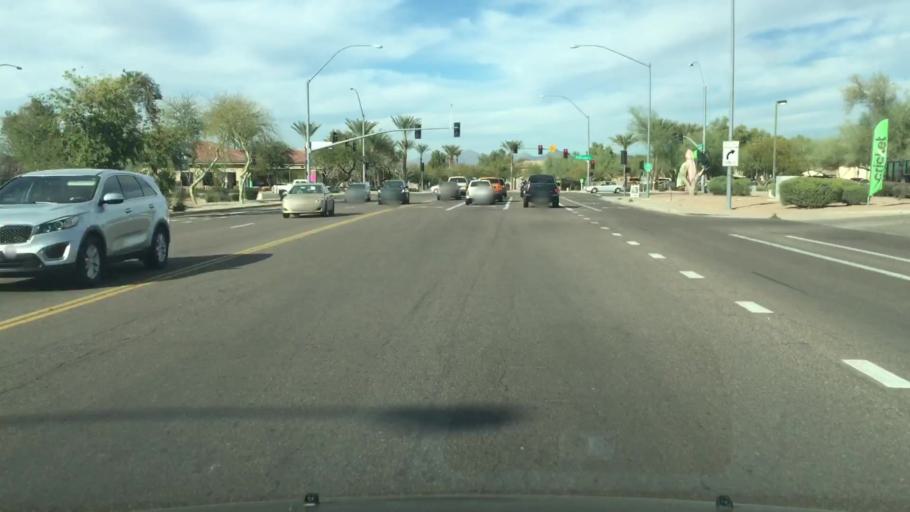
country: US
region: Arizona
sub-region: Maricopa County
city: Mesa
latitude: 33.4505
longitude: -111.8049
